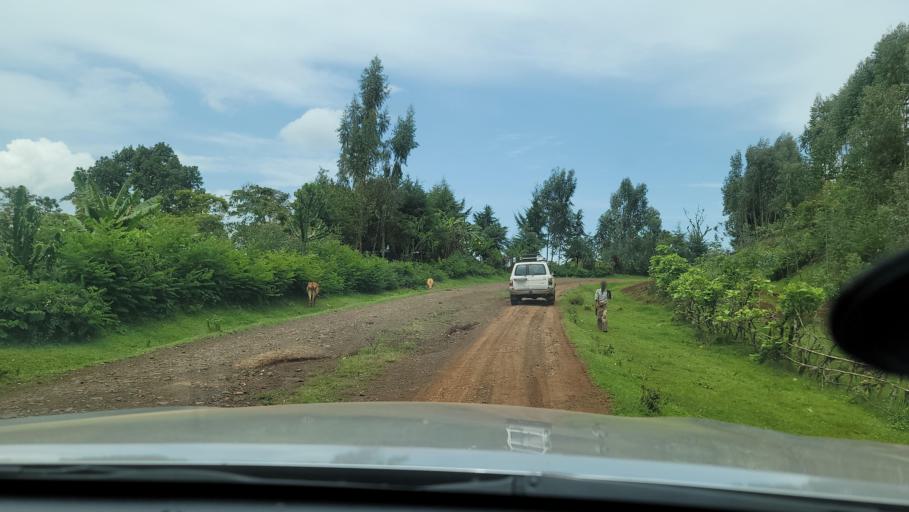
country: ET
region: Southern Nations, Nationalities, and People's Region
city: Bonga
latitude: 7.7024
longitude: 36.2513
